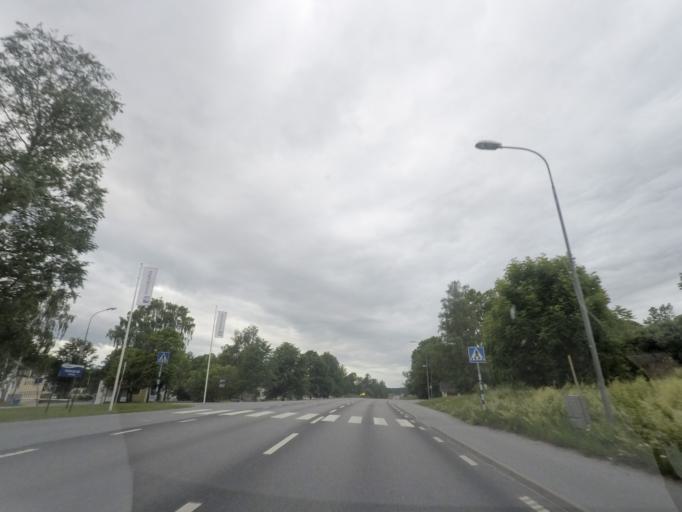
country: SE
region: OErebro
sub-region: Lindesbergs Kommun
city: Lindesberg
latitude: 59.5273
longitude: 15.2835
